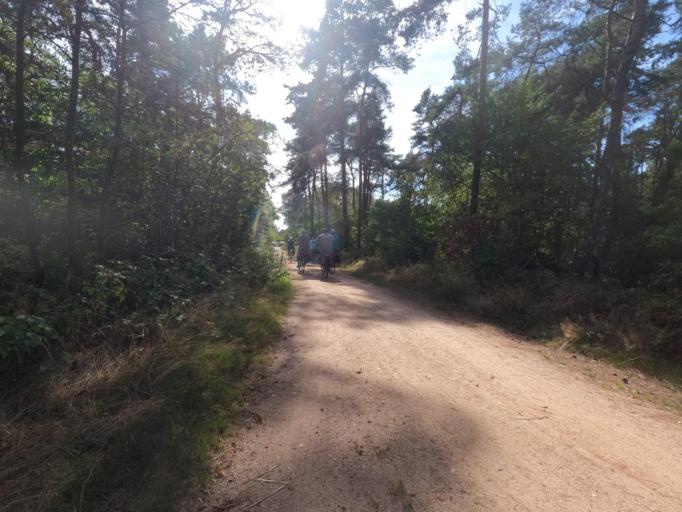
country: NL
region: Limburg
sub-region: Gemeente Beesel
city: Offenbeek
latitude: 51.2753
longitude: 6.1269
